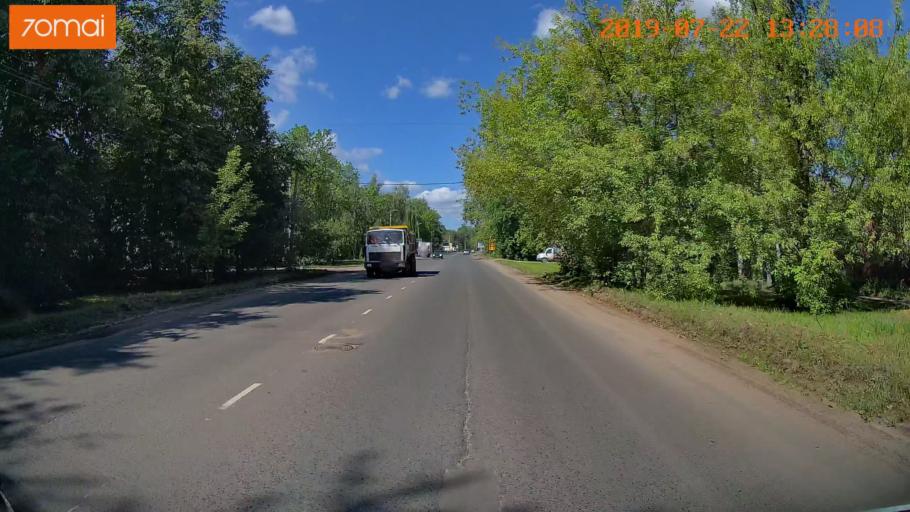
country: RU
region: Ivanovo
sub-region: Gorod Ivanovo
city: Ivanovo
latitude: 57.0397
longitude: 40.9492
